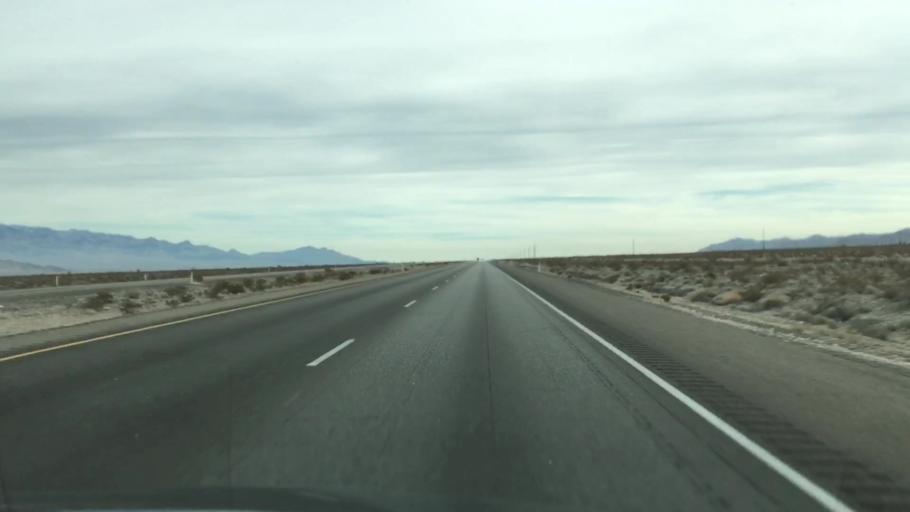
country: US
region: Nevada
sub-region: Nye County
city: Pahrump
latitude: 36.5669
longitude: -115.6233
